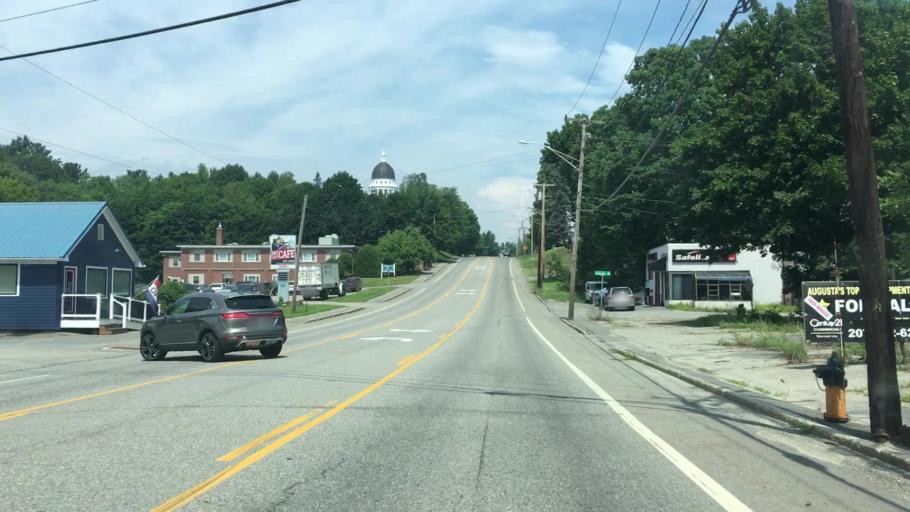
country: US
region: Maine
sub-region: Kennebec County
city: Augusta
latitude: 44.3026
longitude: -69.7820
